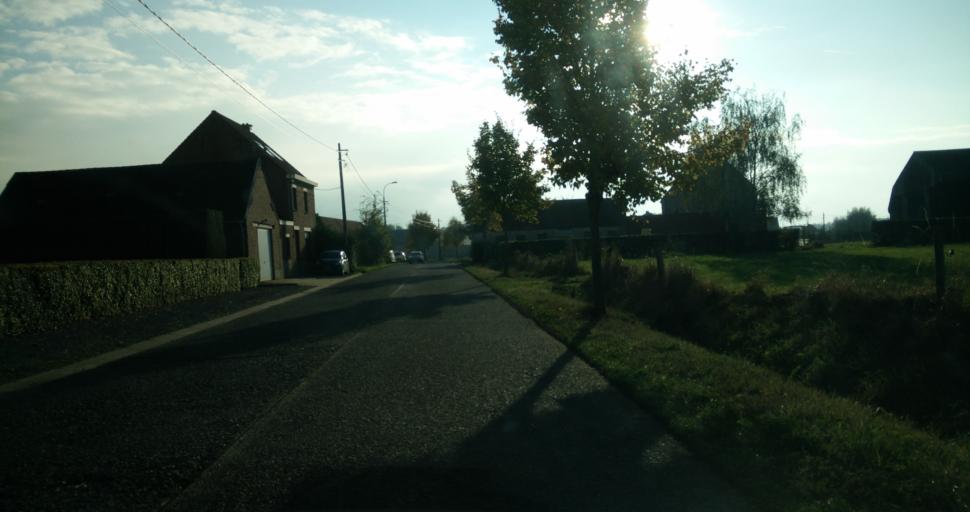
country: BE
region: Flanders
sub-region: Provincie Oost-Vlaanderen
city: Oosterzele
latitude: 50.9131
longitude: 3.7850
